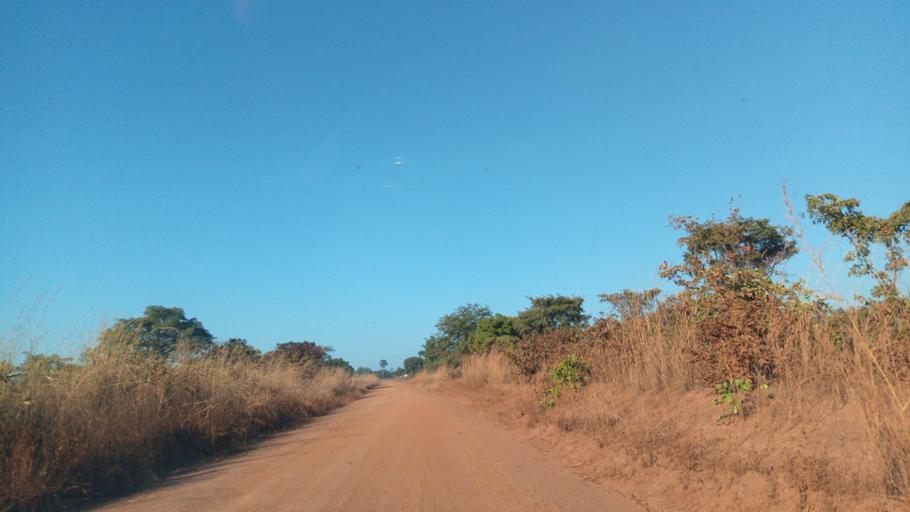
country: ZM
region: Luapula
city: Mwense
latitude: -10.4881
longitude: 28.4876
